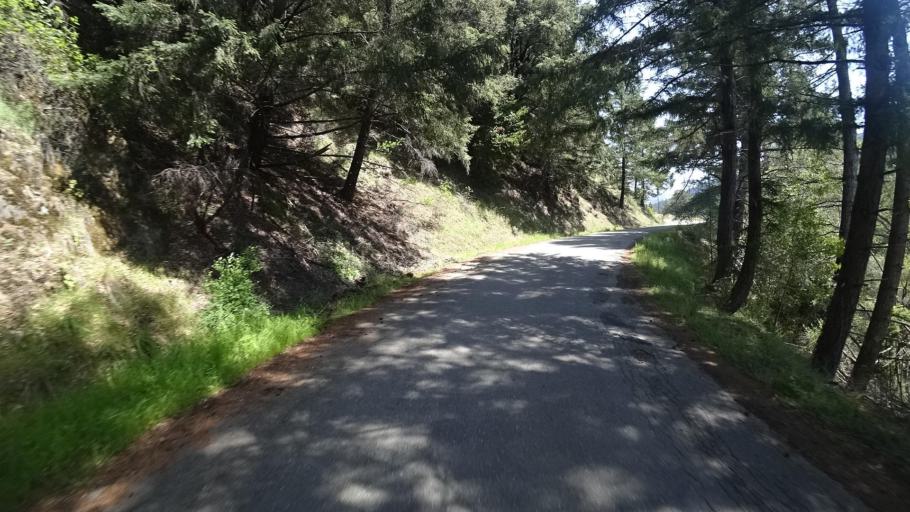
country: US
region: California
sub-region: Humboldt County
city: Redway
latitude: 40.1931
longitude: -123.5474
